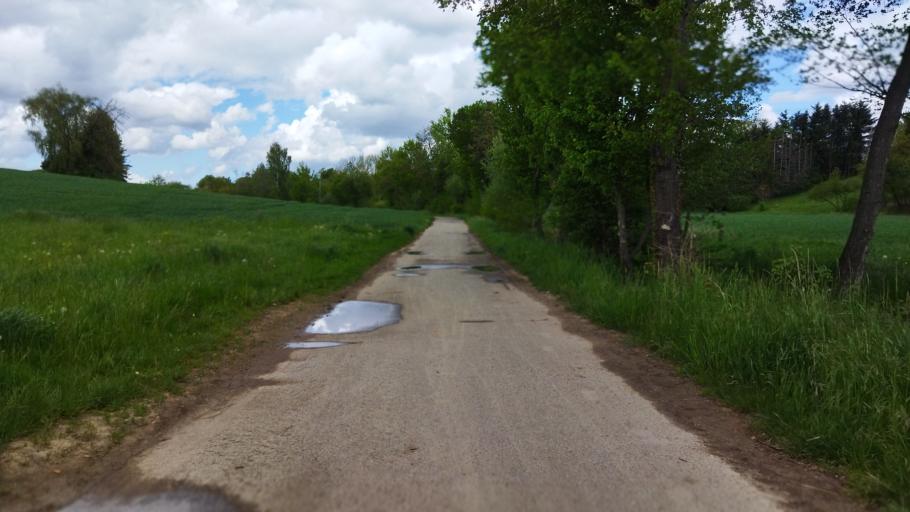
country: DE
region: Baden-Wuerttemberg
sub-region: Regierungsbezirk Stuttgart
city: Leingarten
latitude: 49.1770
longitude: 9.1220
